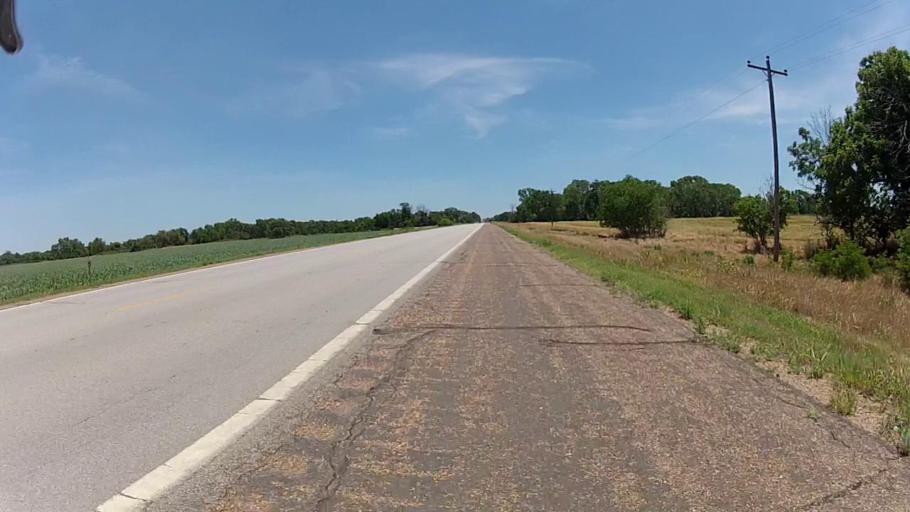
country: US
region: Kansas
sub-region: Barber County
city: Medicine Lodge
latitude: 37.2534
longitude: -98.3346
